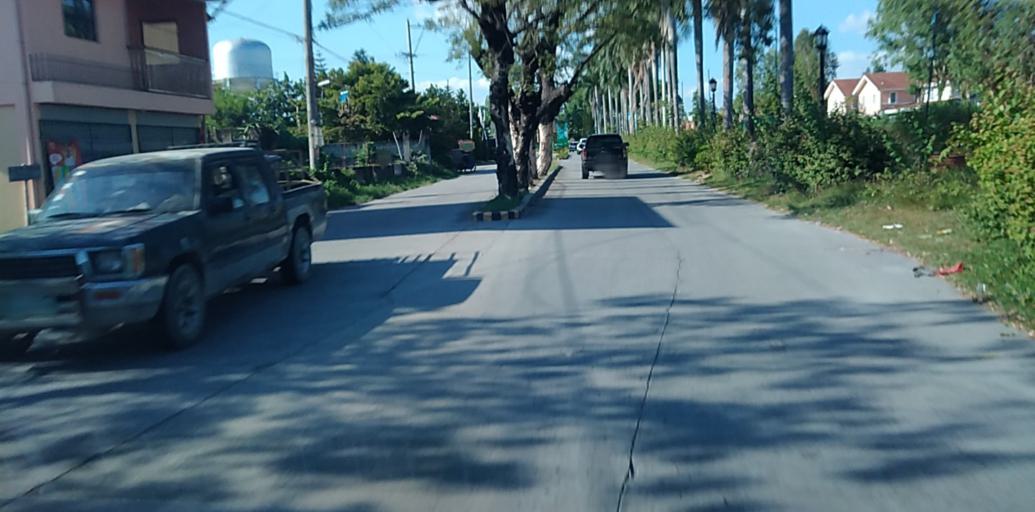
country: PH
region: Central Luzon
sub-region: Province of Pampanga
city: Acli
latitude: 15.1082
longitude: 120.6540
